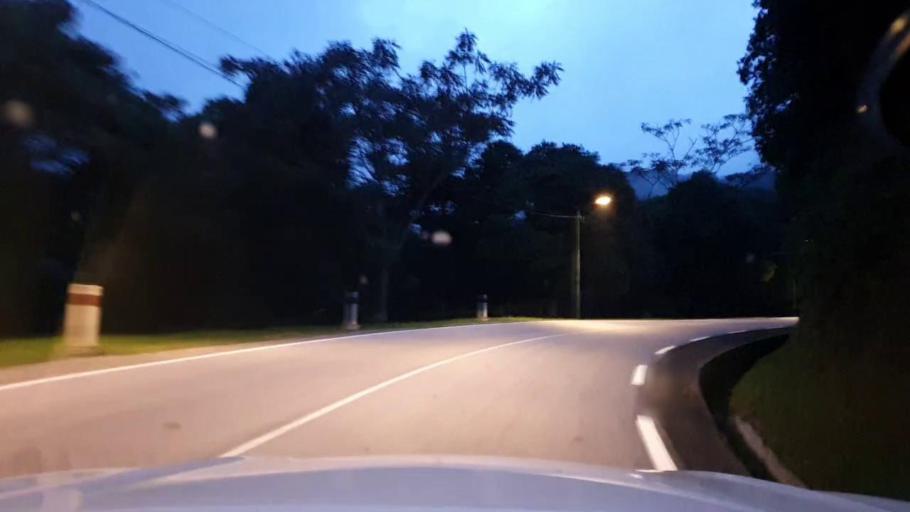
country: RW
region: Southern Province
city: Nzega
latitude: -2.5302
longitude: 29.3875
